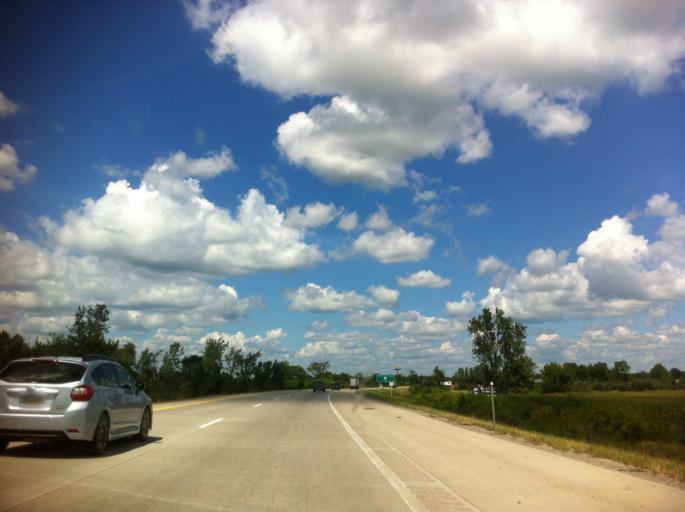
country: US
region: Ohio
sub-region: Lucas County
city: Sylvania
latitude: 41.7856
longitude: -83.6957
